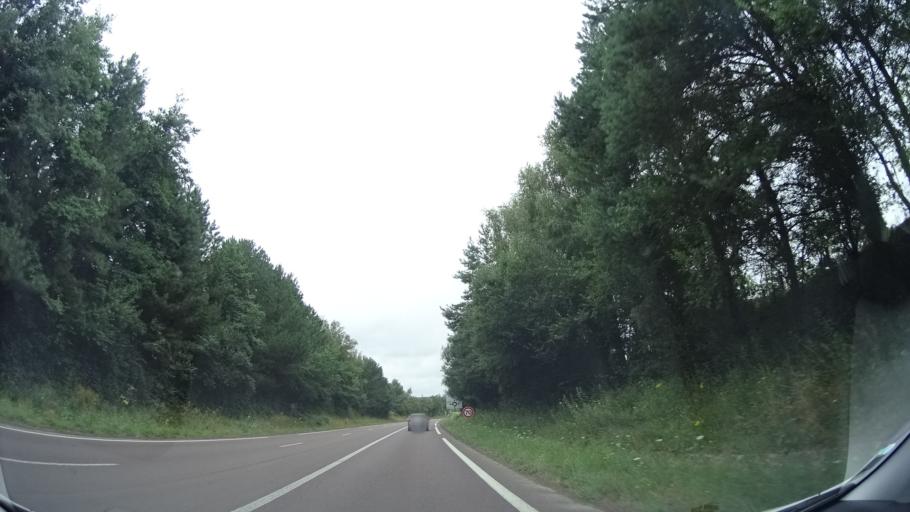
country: FR
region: Lower Normandy
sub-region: Departement de la Manche
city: La Haye-du-Puits
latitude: 49.2924
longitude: -1.5583
